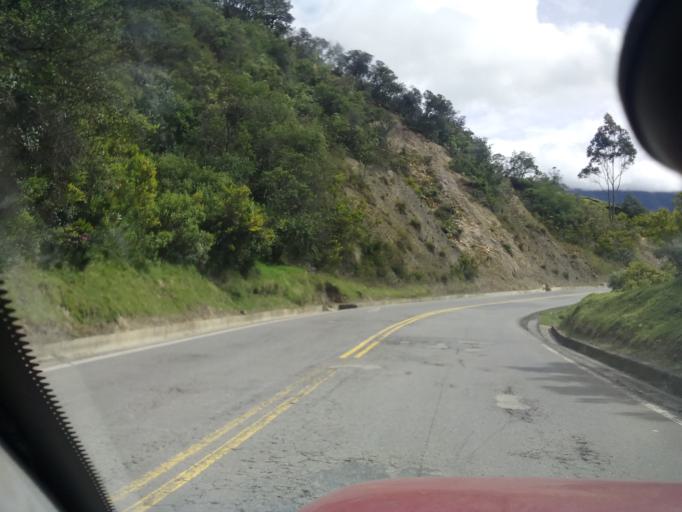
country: CO
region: Boyaca
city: Combita
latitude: 5.6771
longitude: -73.3617
